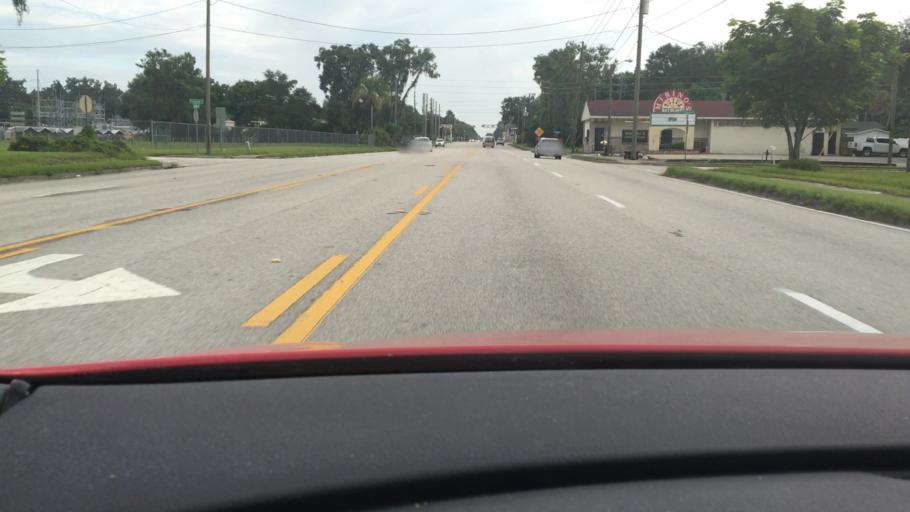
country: US
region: Florida
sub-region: Volusia County
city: West DeLand
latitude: 29.0304
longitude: -81.3243
